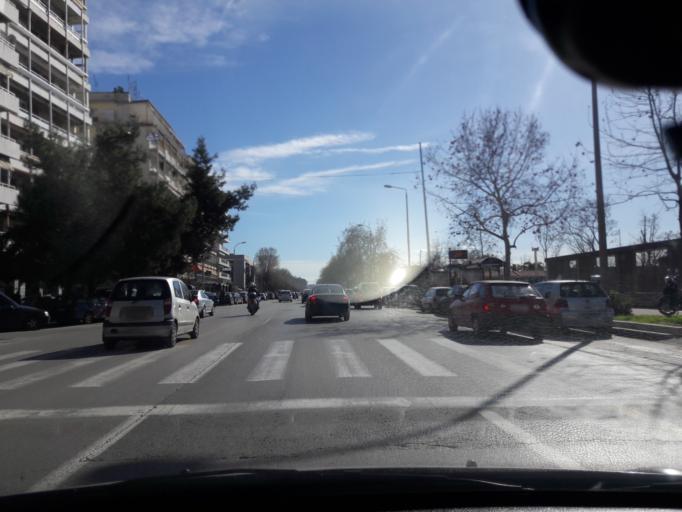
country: GR
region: Central Macedonia
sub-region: Nomos Thessalonikis
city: Triandria
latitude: 40.6103
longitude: 22.9517
